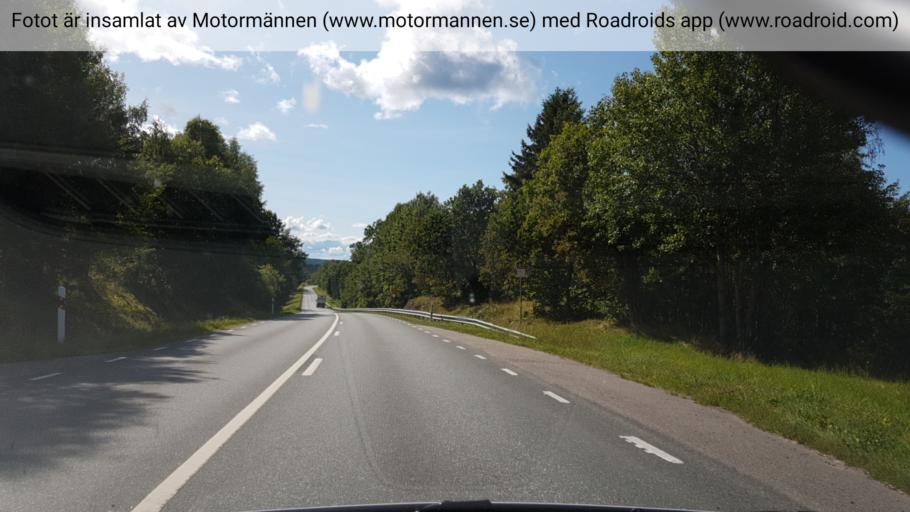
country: SE
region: Joenkoeping
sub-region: Jonkopings Kommun
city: Asa
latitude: 58.0063
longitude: 14.6252
